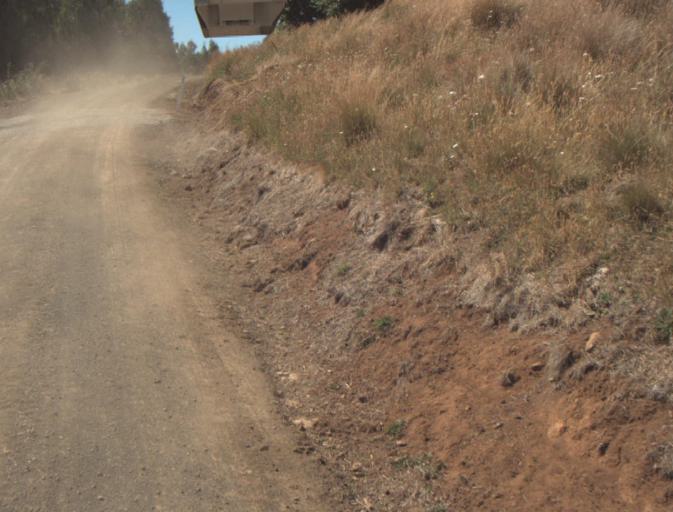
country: AU
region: Tasmania
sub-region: Dorset
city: Scottsdale
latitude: -41.3477
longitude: 147.4536
